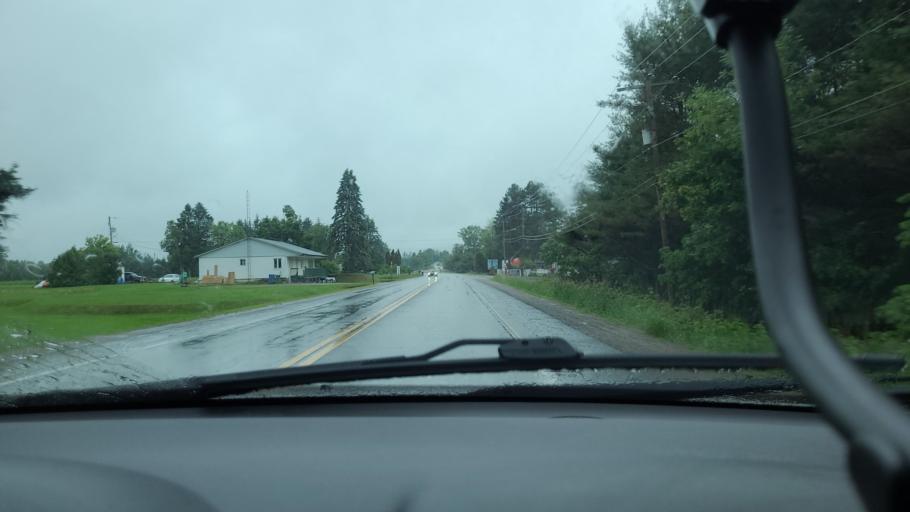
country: CA
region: Quebec
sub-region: Outaouais
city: Saint-Andre-Avellin
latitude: 45.8073
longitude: -75.0637
